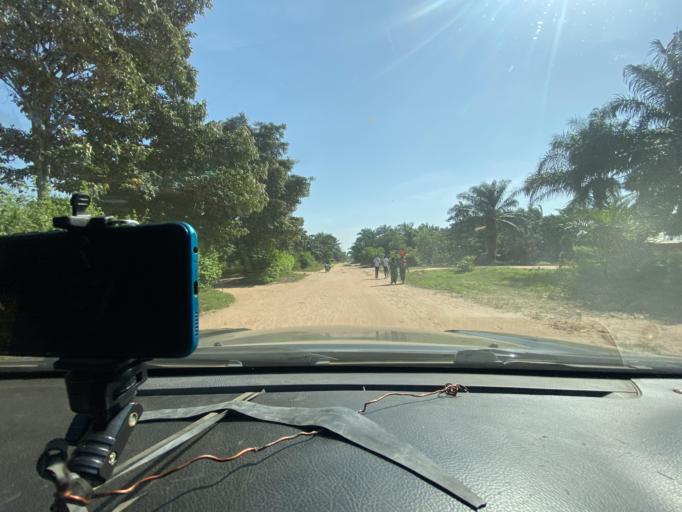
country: CD
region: Kasai-Oriental
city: Kabinda
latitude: -6.1231
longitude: 24.5269
